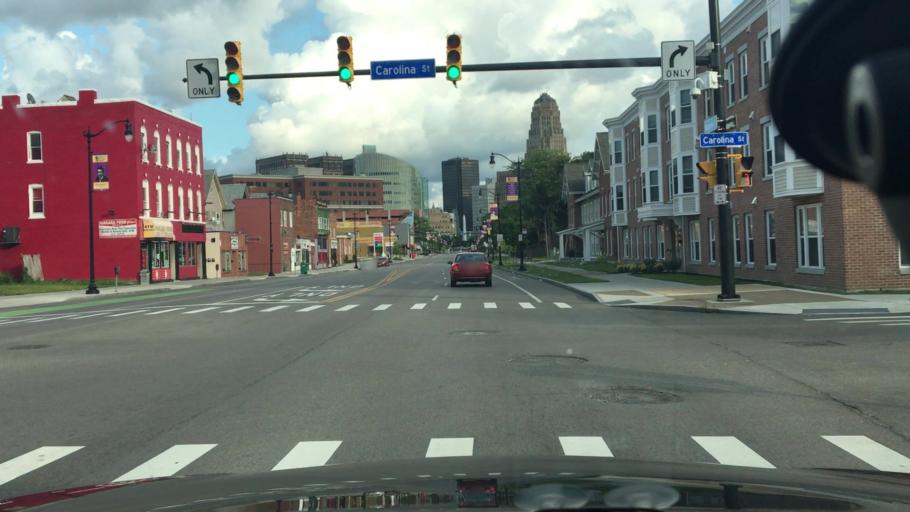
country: US
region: New York
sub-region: Erie County
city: Buffalo
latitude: 42.8919
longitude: -78.8834
